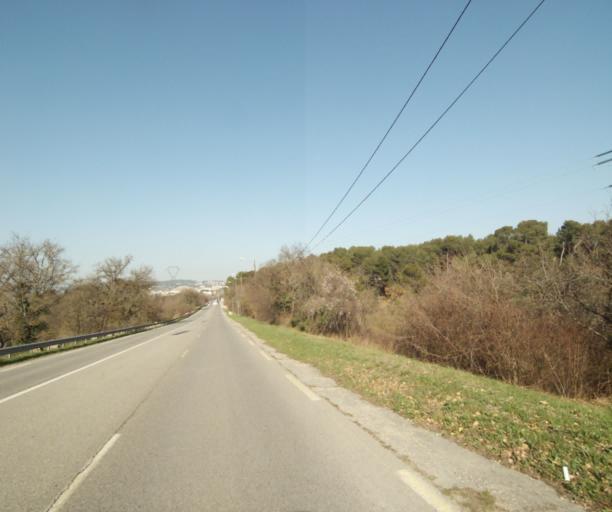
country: FR
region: Provence-Alpes-Cote d'Azur
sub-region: Departement des Bouches-du-Rhone
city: Aix-en-Provence
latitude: 43.4999
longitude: 5.4344
